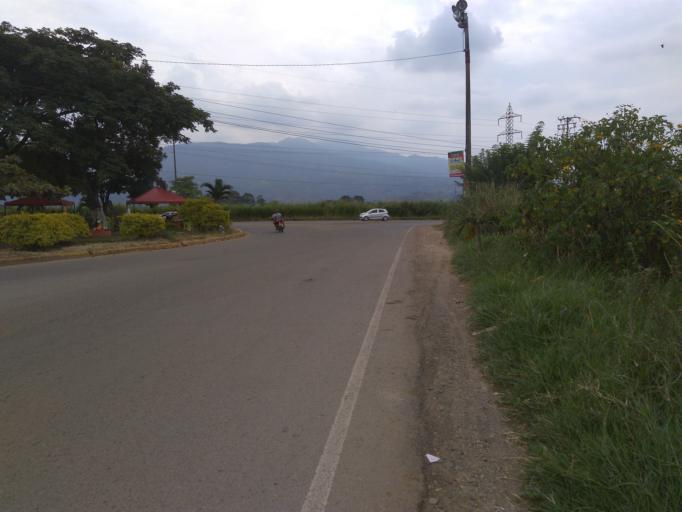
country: CO
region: Valle del Cauca
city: Jamundi
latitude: 3.2598
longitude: -76.5584
